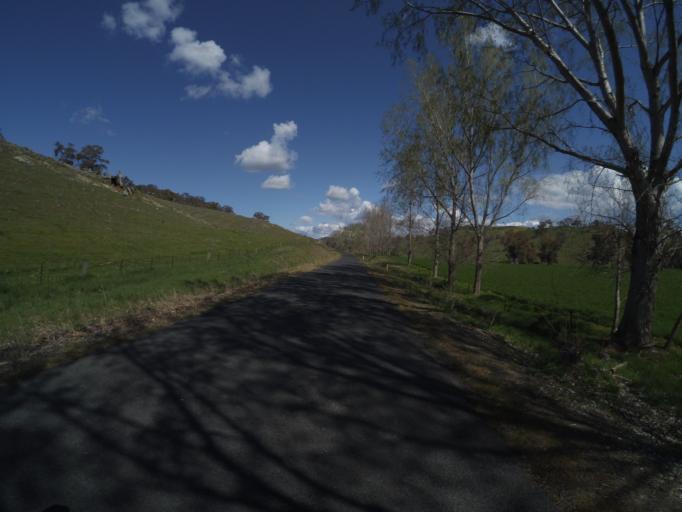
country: AU
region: New South Wales
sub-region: Yass Valley
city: Murrumbateman
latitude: -35.0419
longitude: 148.8402
